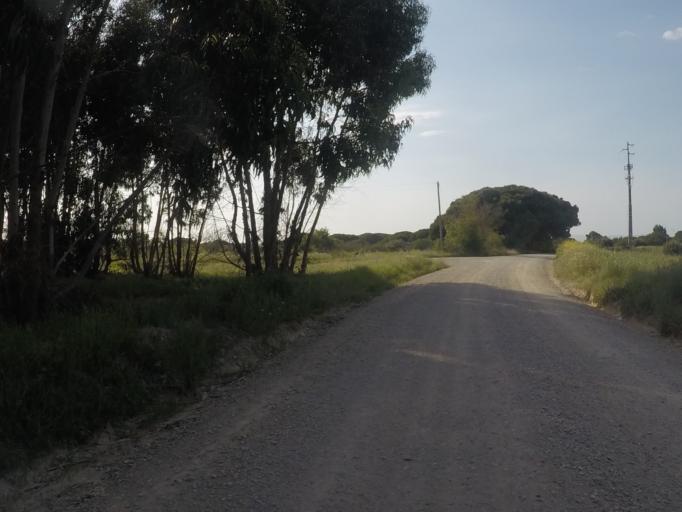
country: PT
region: Setubal
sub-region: Sesimbra
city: Sesimbra
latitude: 38.4429
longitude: -9.1966
